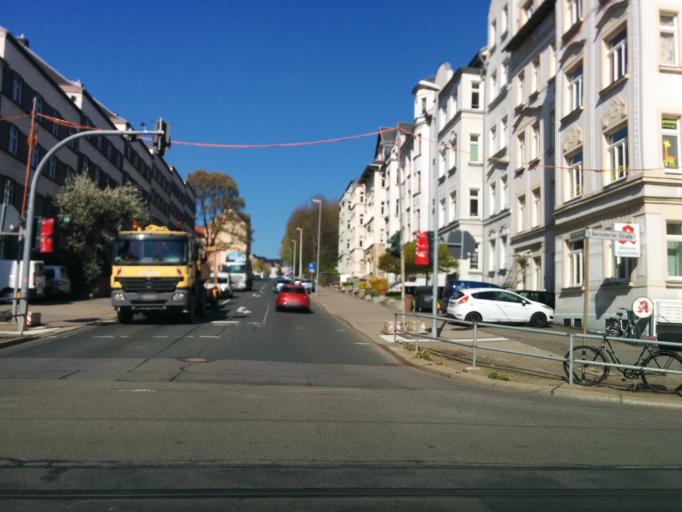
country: DE
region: Saxony
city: Chemnitz
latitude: 50.8179
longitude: 12.9391
